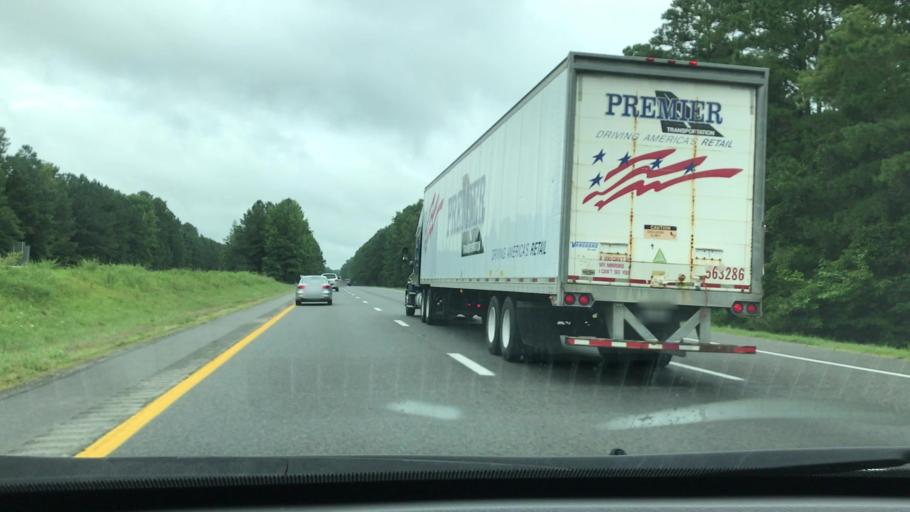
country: US
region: Virginia
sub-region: City of Emporia
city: Emporia
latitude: 36.7370
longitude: -77.5195
